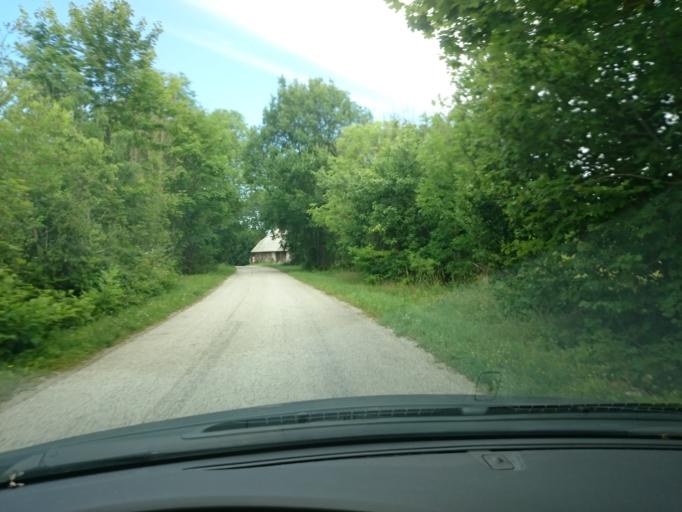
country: EE
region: Laeaene
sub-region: Ridala Parish
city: Uuemoisa
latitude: 58.9885
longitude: 23.6674
